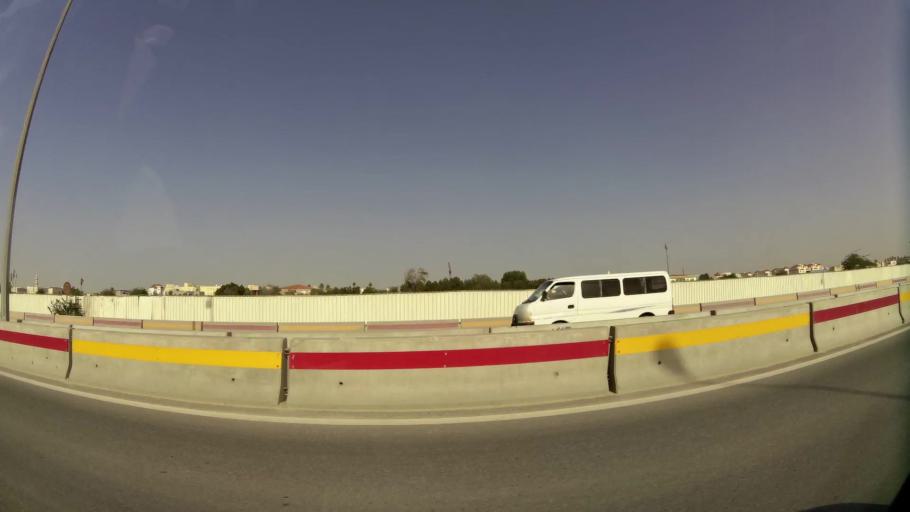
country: QA
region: Baladiyat ar Rayyan
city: Ar Rayyan
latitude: 25.3263
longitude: 51.4478
